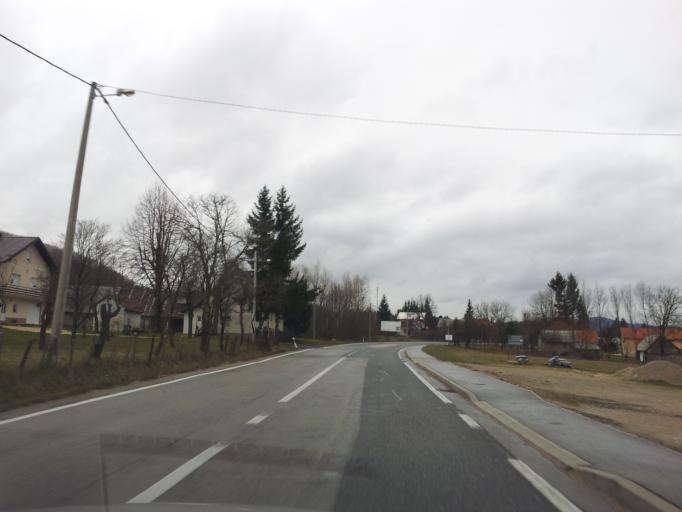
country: HR
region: Licko-Senjska
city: Jezerce
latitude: 44.7597
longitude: 15.6944
